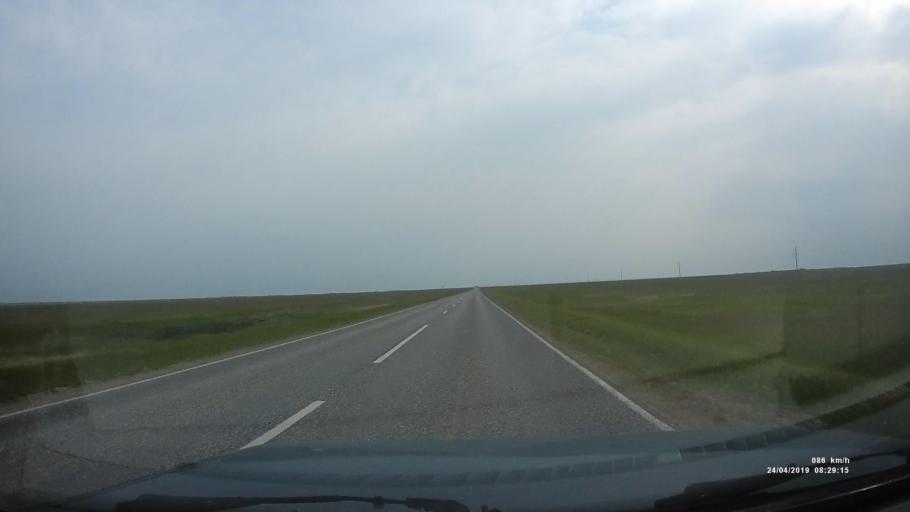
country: RU
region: Kalmykiya
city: Priyutnoye
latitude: 46.1508
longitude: 43.8279
